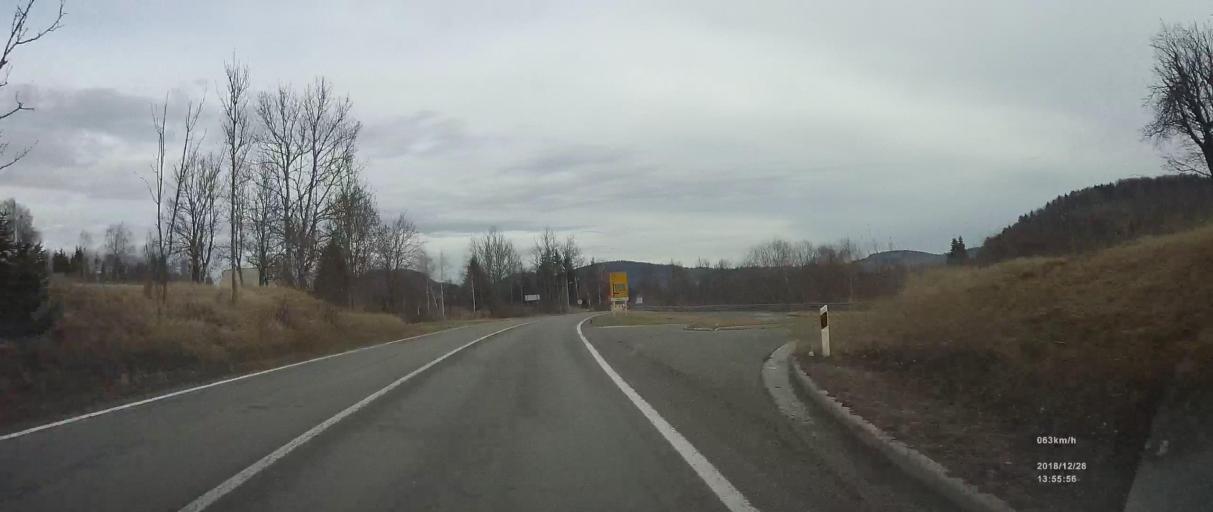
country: HR
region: Primorsko-Goranska
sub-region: Grad Delnice
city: Delnice
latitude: 45.3847
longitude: 14.8818
